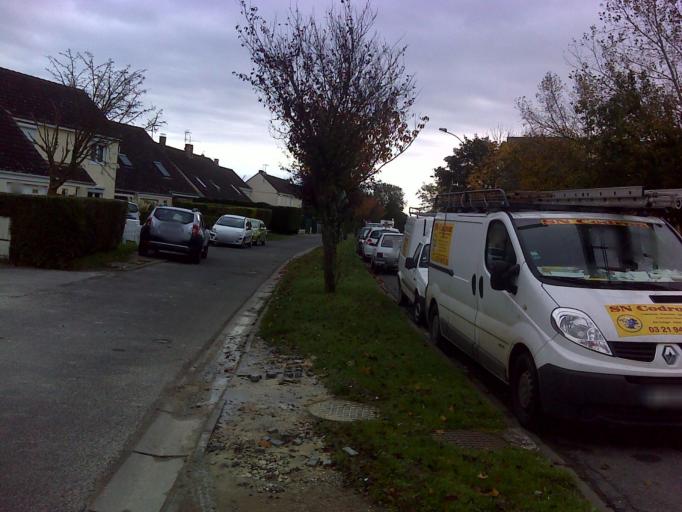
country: FR
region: Nord-Pas-de-Calais
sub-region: Departement du Pas-de-Calais
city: Etaples
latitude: 50.5200
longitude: 1.6499
